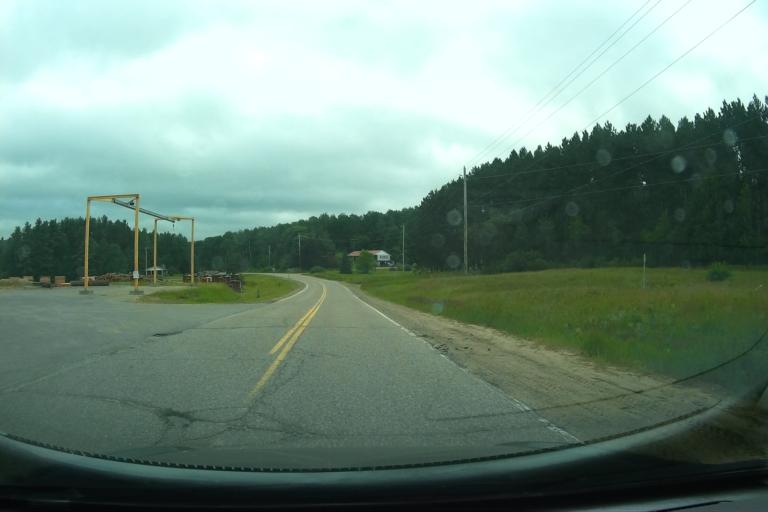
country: CA
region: Ontario
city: Pembroke
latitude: 45.4896
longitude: -77.1952
